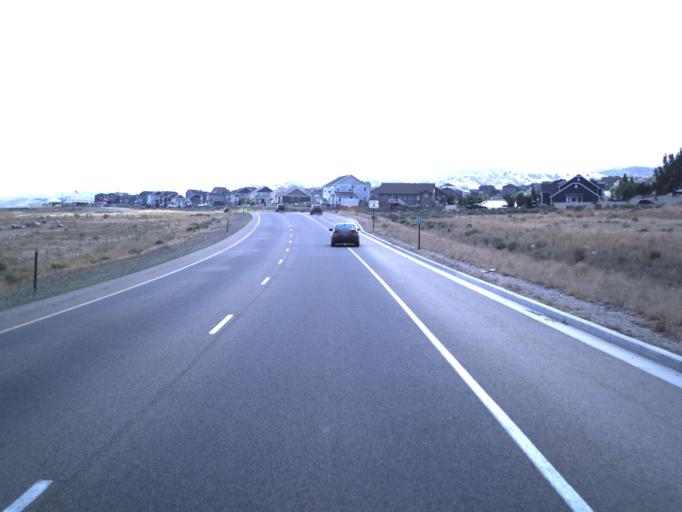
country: US
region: Utah
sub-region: Salt Lake County
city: Herriman
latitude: 40.4950
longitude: -112.0047
